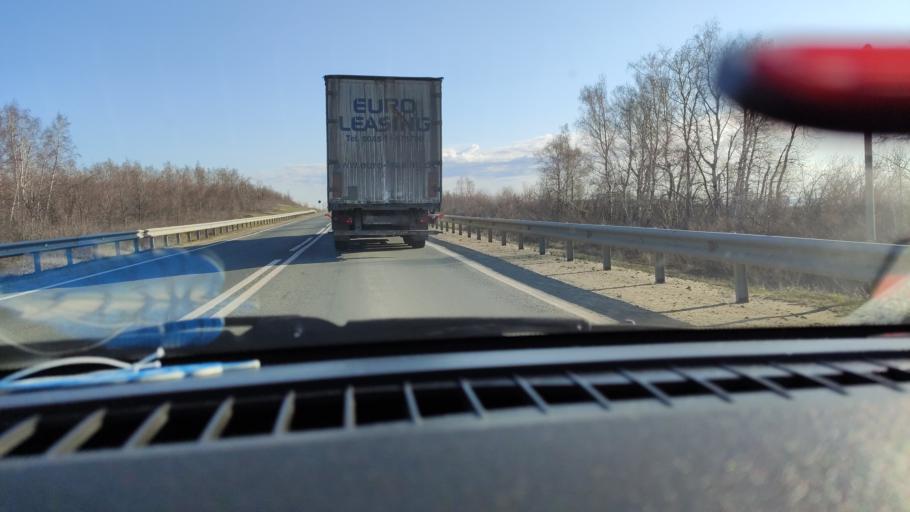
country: RU
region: Saratov
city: Dukhovnitskoye
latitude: 52.6777
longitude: 48.2291
